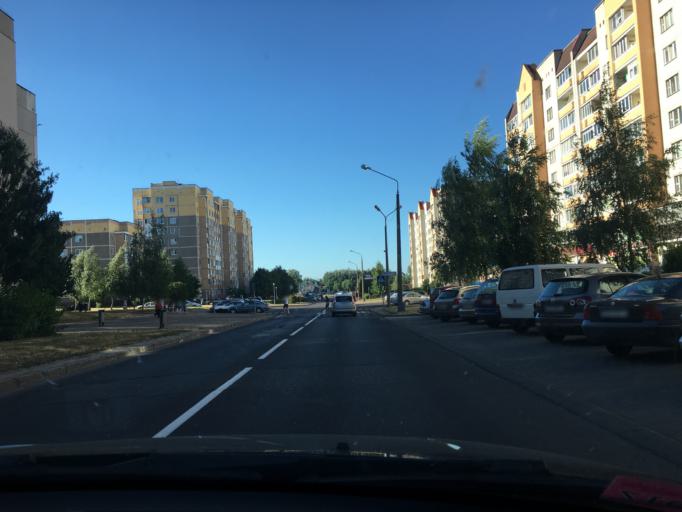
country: BY
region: Grodnenskaya
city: Hrodna
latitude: 53.7130
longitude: 23.8496
